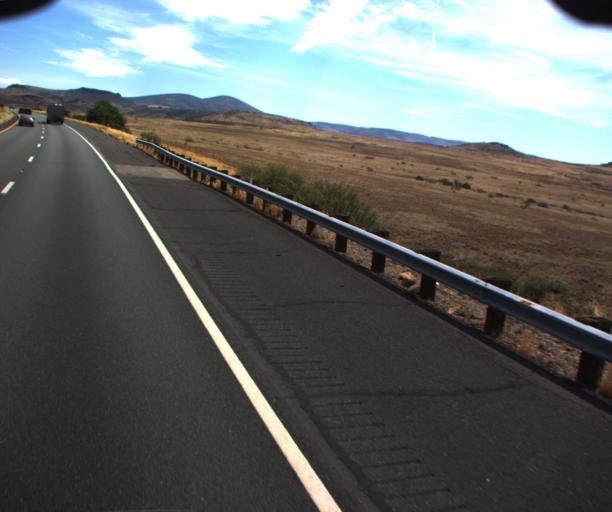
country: US
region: Arizona
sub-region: Yavapai County
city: Cordes Lakes
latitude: 34.4261
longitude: -112.0398
